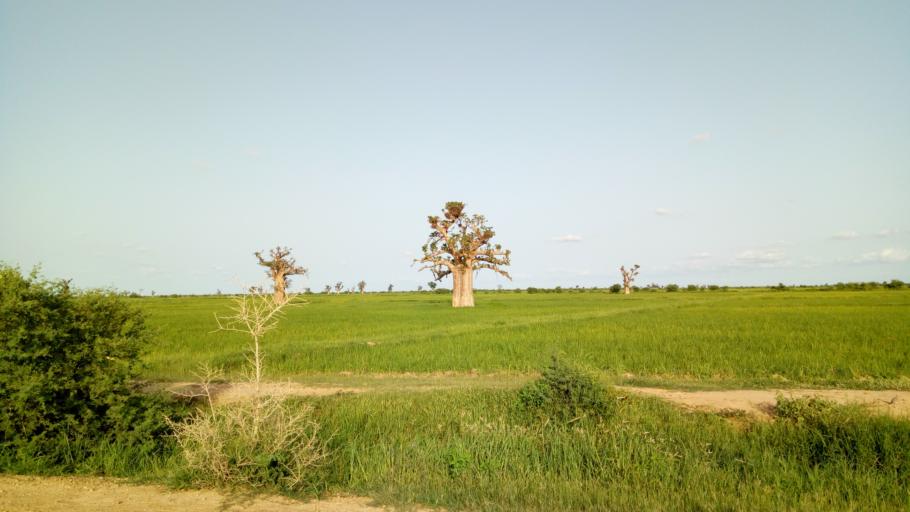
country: ML
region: Segou
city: Niono
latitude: 14.2960
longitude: -5.9434
